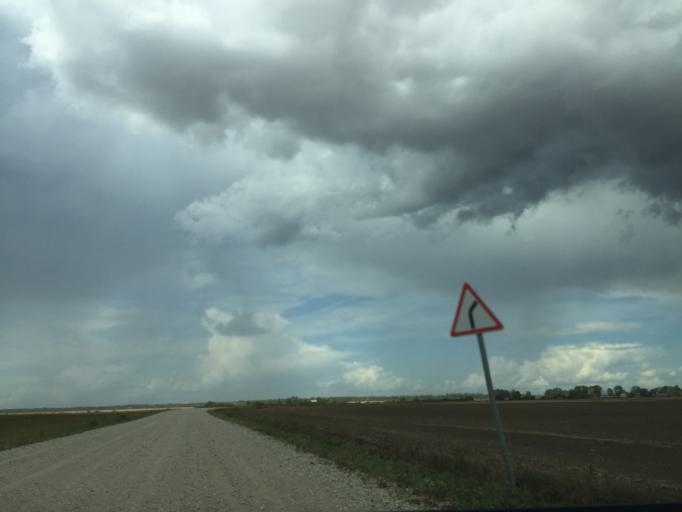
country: LT
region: Siauliu apskritis
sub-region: Joniskis
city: Joniskis
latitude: 56.2773
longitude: 23.7359
